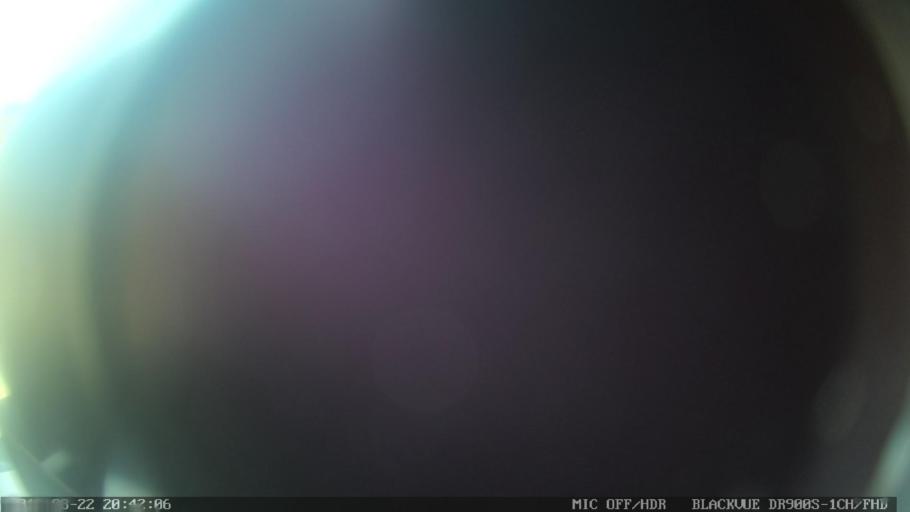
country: PT
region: Castelo Branco
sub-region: Proenca-A-Nova
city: Proenca-a-Nova
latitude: 39.6918
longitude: -7.8122
